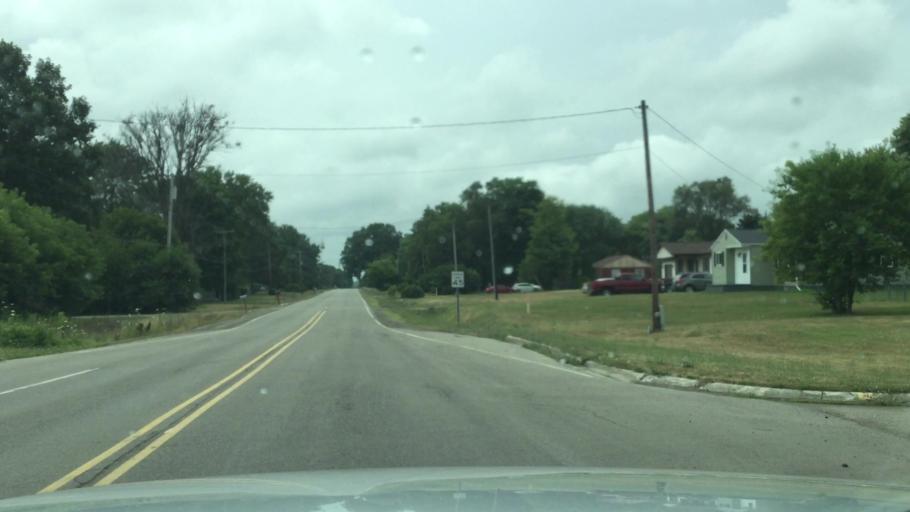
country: US
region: Michigan
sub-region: Genesee County
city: Beecher
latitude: 43.0915
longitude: -83.6175
